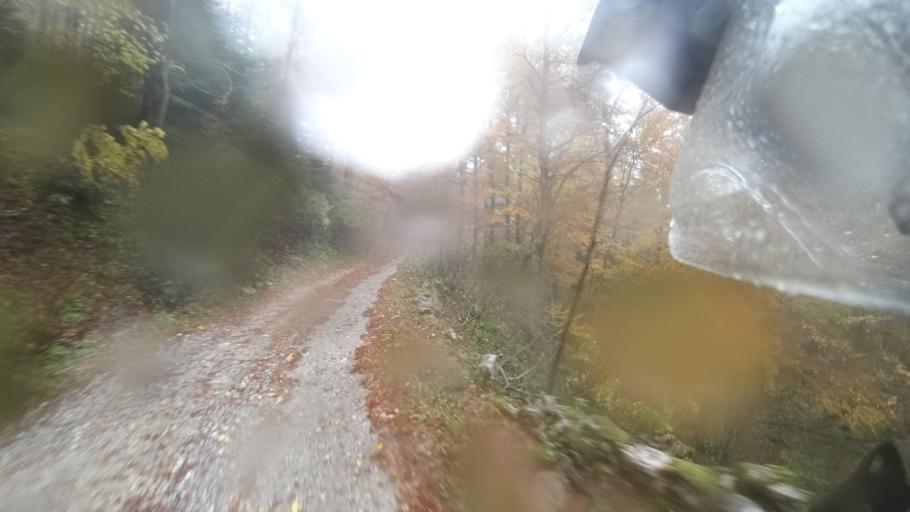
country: HR
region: Primorsko-Goranska
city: Vrbovsko
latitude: 45.2961
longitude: 14.9373
